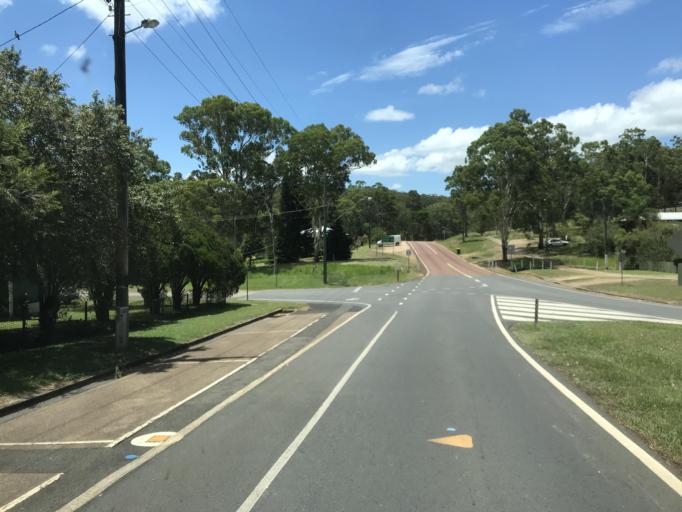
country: AU
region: Queensland
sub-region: Tablelands
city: Ravenshoe
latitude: -17.6038
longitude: 145.4802
